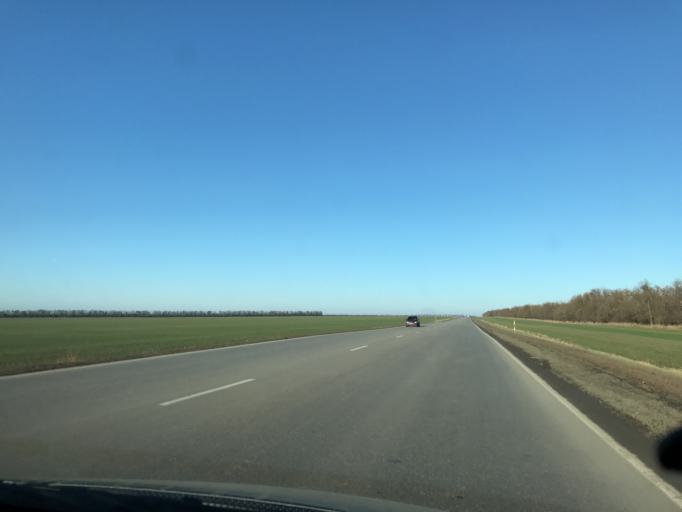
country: RU
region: Rostov
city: Kagal'nitskaya
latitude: 46.9066
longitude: 40.1176
